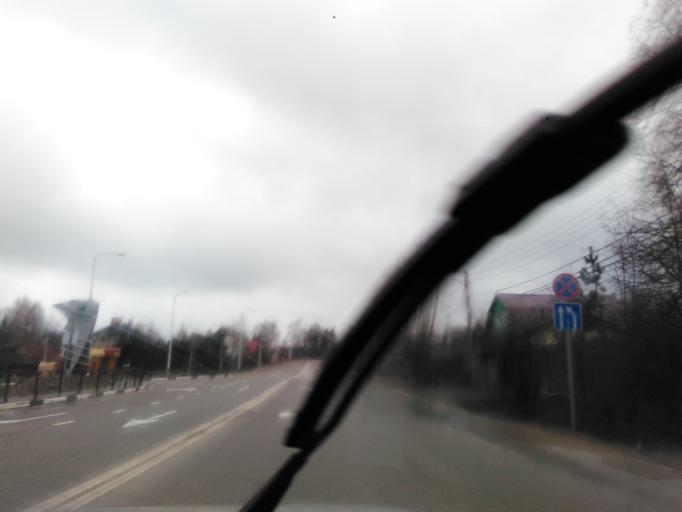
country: RU
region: Moskovskaya
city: Rozhdestveno
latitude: 55.8427
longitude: 37.0011
